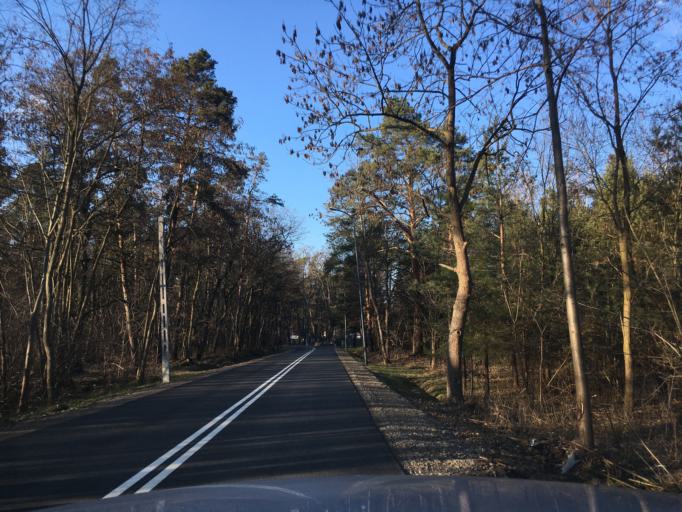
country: PL
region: Lodz Voivodeship
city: Zabia Wola
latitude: 52.0491
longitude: 20.7396
